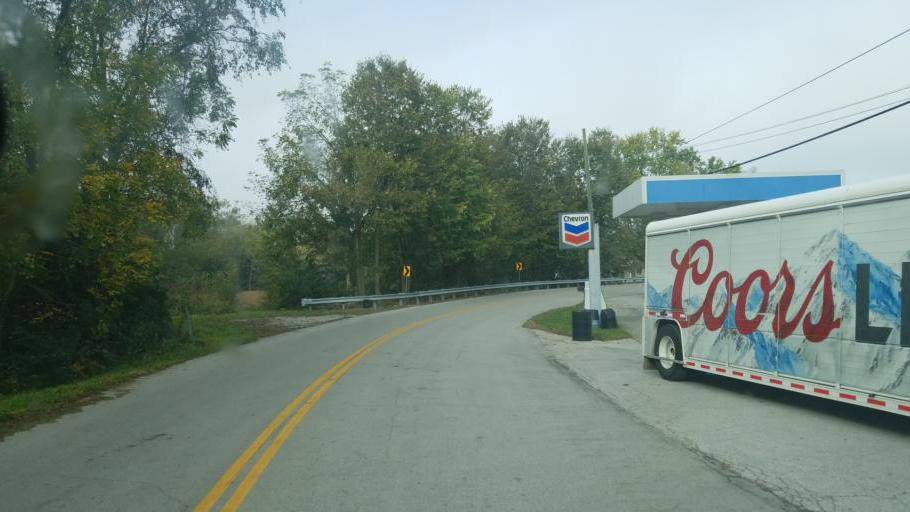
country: US
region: Kentucky
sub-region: Mason County
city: Maysville
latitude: 38.5492
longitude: -83.7660
